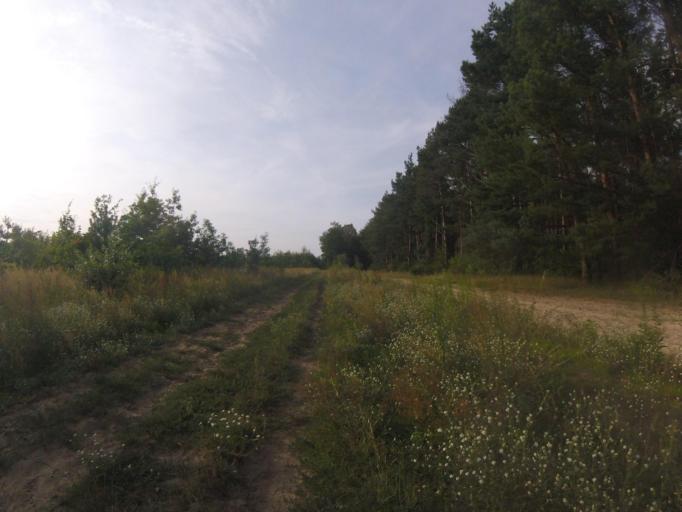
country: DE
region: Berlin
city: Lichtenrade
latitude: 52.3571
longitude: 13.4536
